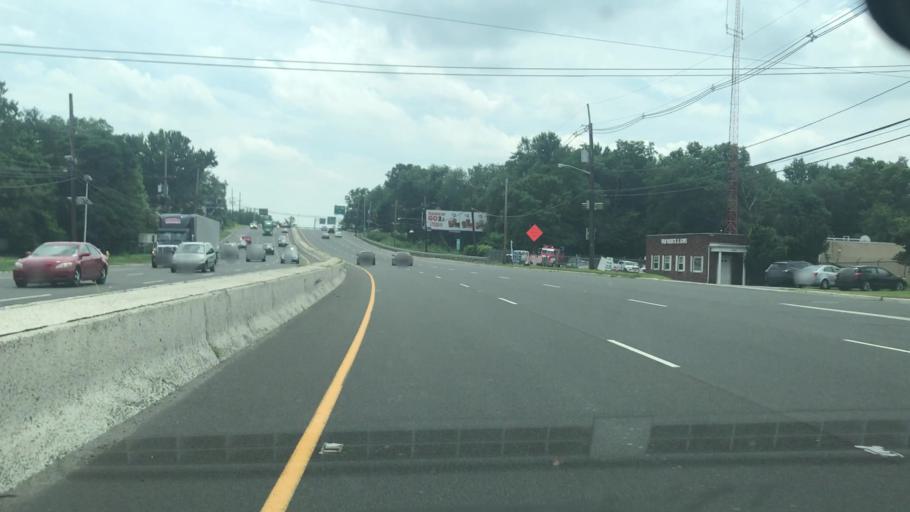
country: US
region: New Jersey
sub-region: Passaic County
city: Wayne
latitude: 40.9209
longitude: -74.2679
